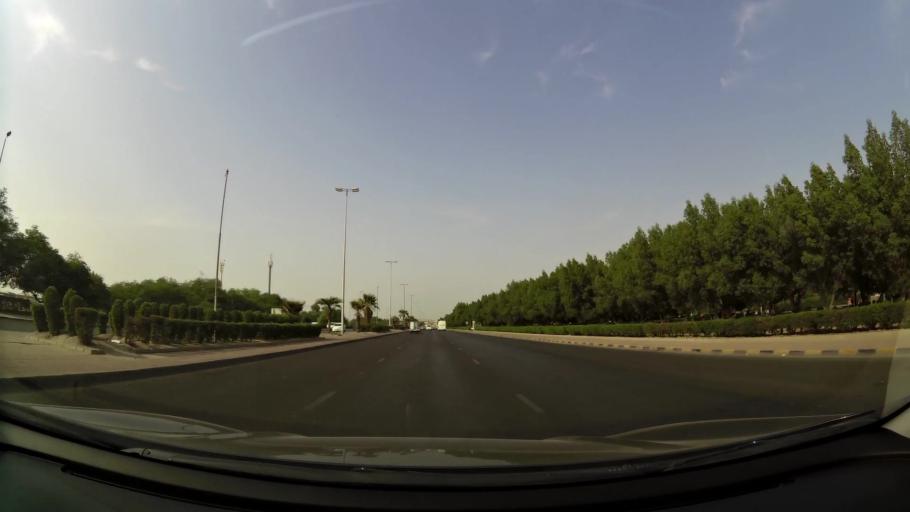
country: KW
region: Al Asimah
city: Ar Rabiyah
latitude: 29.3107
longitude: 47.9622
